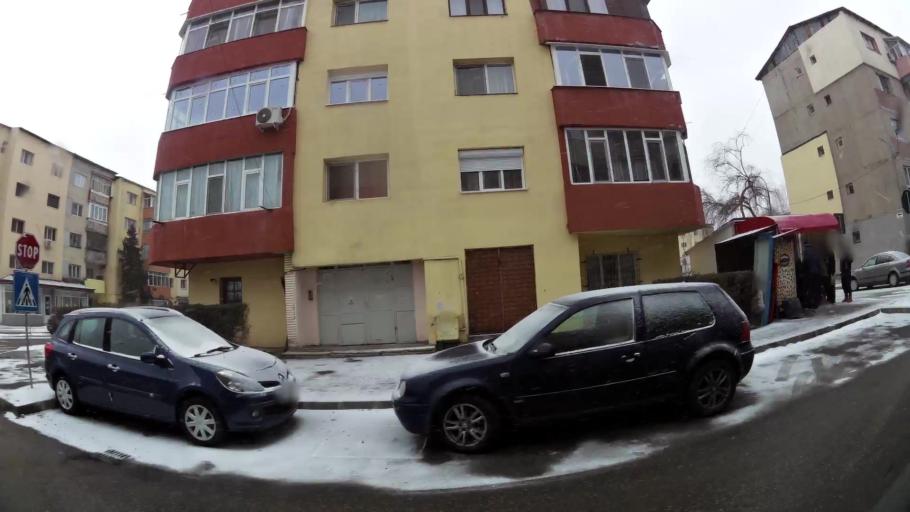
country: RO
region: Dambovita
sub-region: Municipiul Targoviste
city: Targoviste
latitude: 44.9160
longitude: 25.4765
